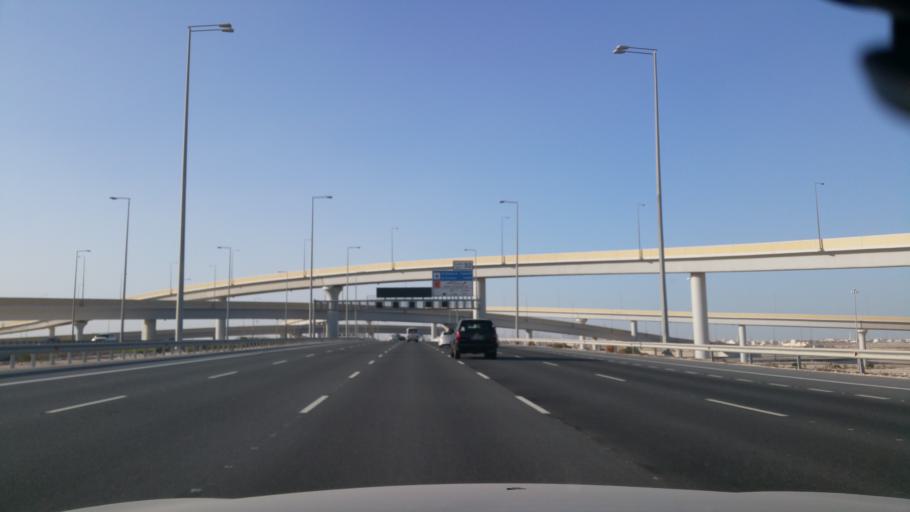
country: QA
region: Al Wakrah
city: Al Wukayr
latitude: 25.2009
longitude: 51.5425
